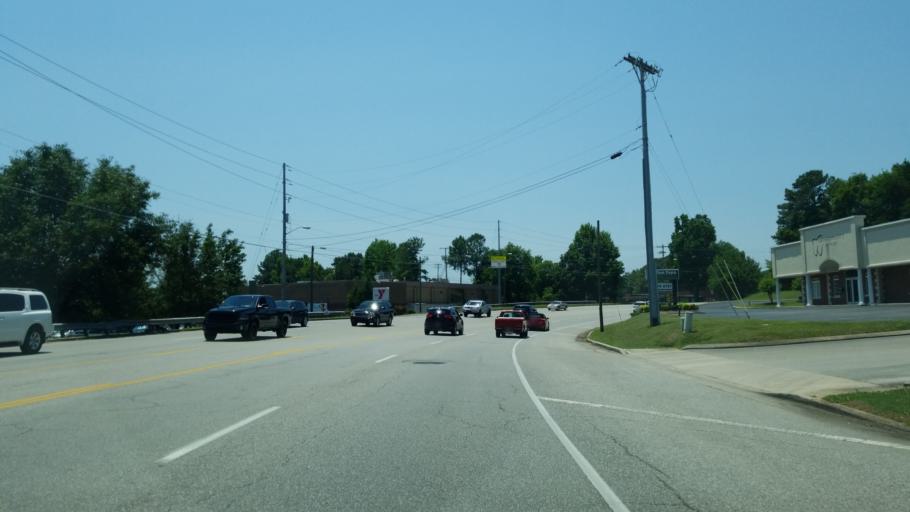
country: US
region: Tennessee
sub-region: Hamilton County
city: Red Bank
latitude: 35.1159
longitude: -85.2513
